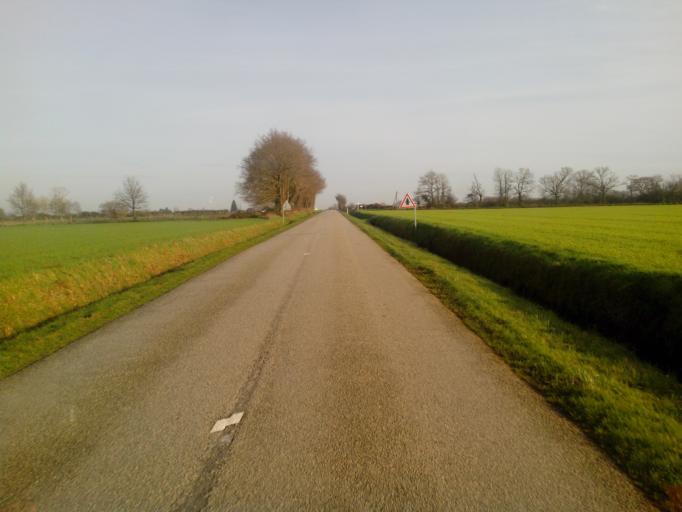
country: FR
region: Brittany
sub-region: Departement du Morbihan
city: Mauron
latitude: 48.0834
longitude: -2.3116
